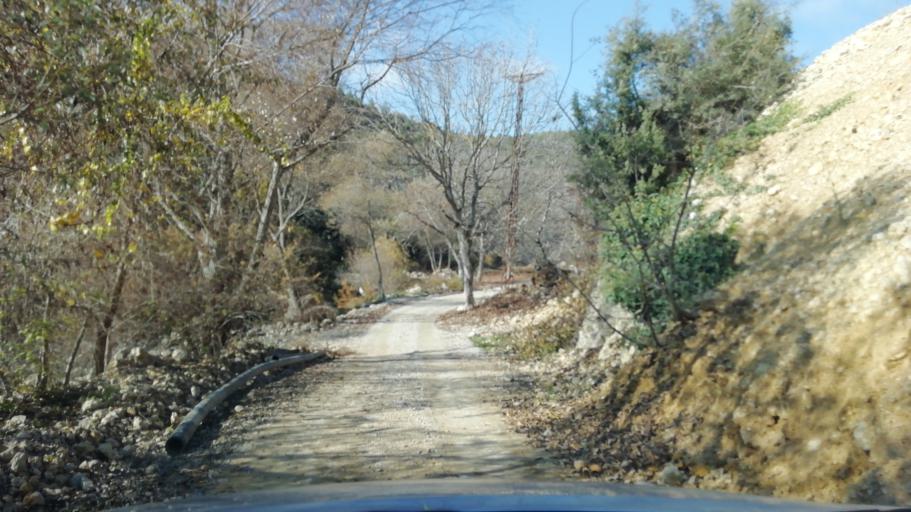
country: TR
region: Karabuk
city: Safranbolu
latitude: 41.2357
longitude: 32.7848
